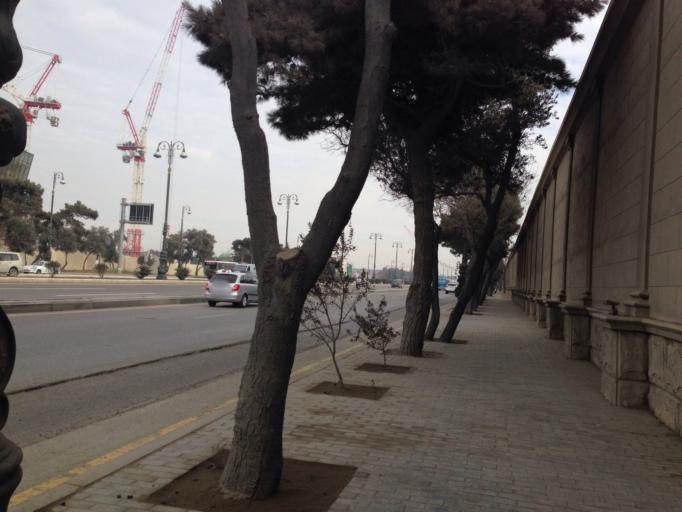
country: AZ
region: Baki
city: Baku
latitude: 40.4085
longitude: 49.8918
